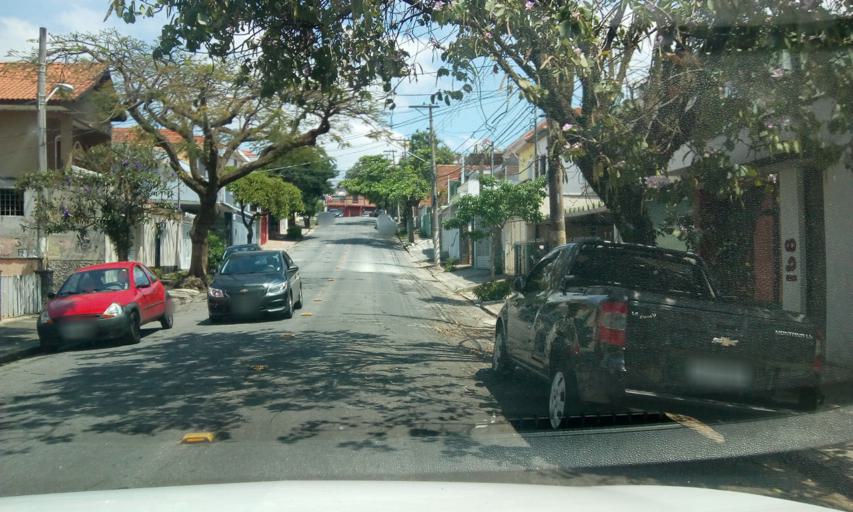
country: BR
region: Sao Paulo
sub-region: Sao Paulo
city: Sao Paulo
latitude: -23.5333
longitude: -46.6963
